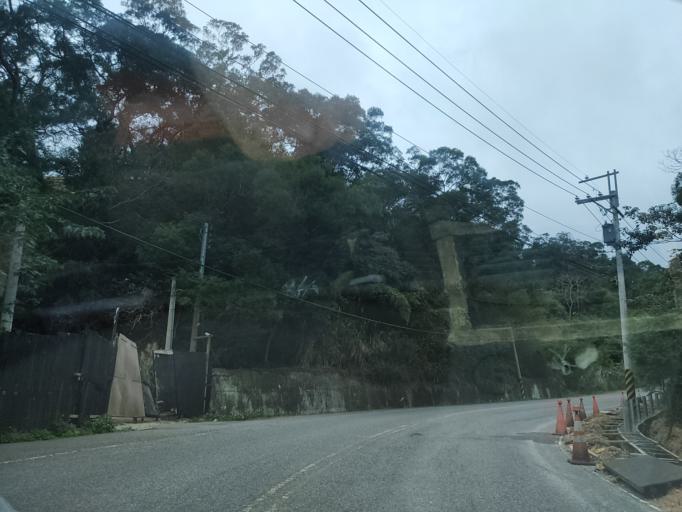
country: TW
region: Taiwan
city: Fengyuan
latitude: 24.3689
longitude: 120.7732
